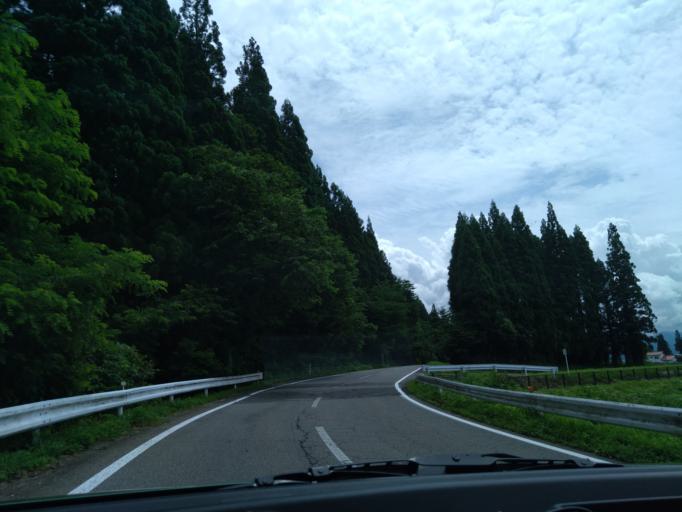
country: JP
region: Akita
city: Kakunodatemachi
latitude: 39.5456
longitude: 140.6361
